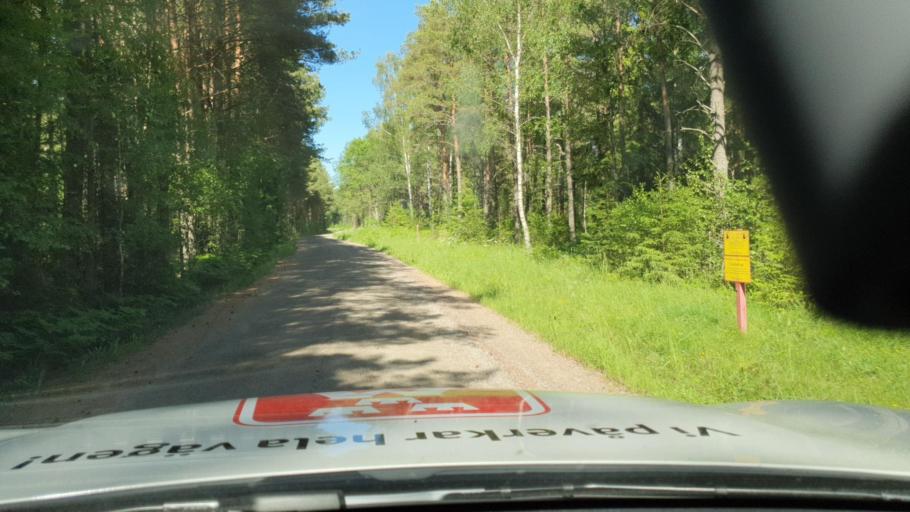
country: SE
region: Vaestra Goetaland
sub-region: Skovde Kommun
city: Skultorp
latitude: 58.3134
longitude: 13.8637
